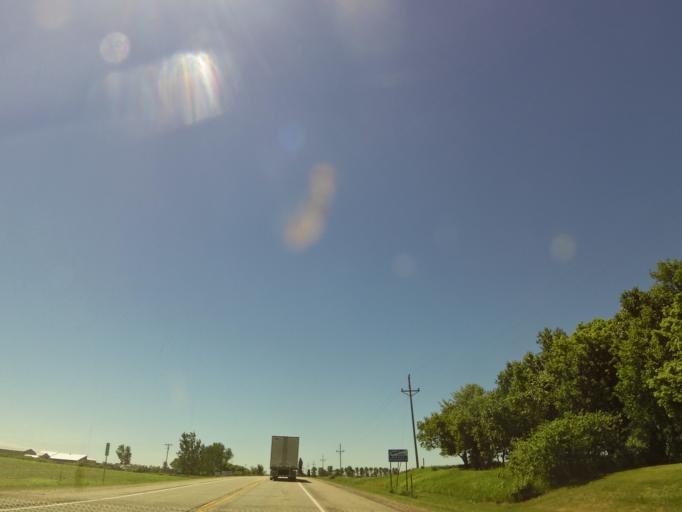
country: US
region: Minnesota
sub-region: Mahnomen County
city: Mahnomen
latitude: 47.1711
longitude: -95.9329
